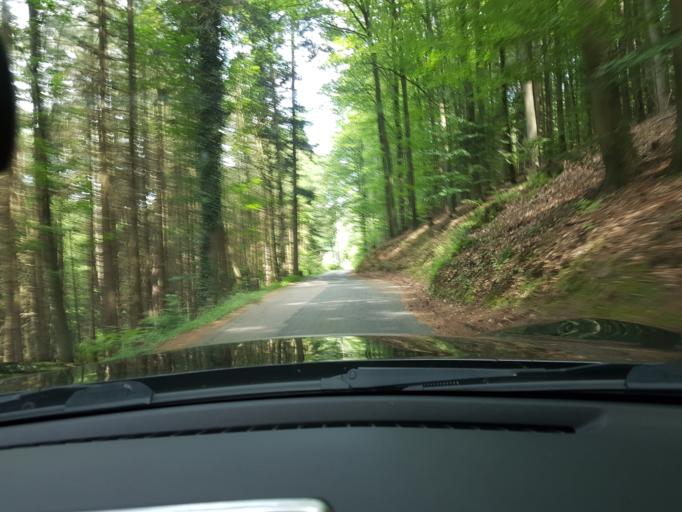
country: DE
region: Hesse
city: Hirschhorn
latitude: 49.4520
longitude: 8.8977
